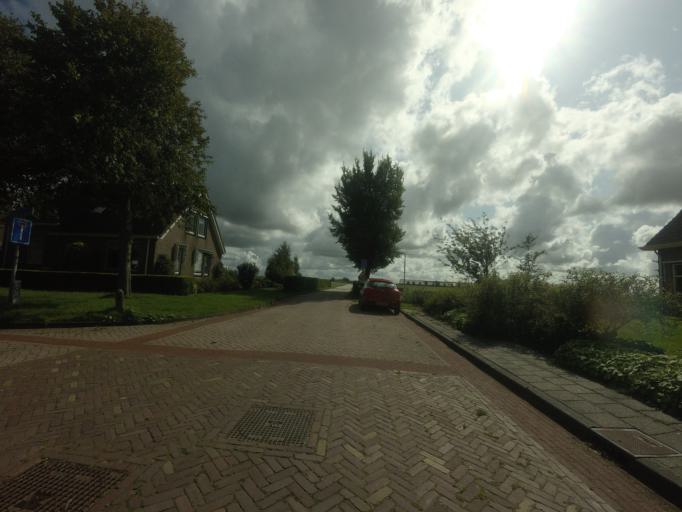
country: NL
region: Friesland
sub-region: Sudwest Fryslan
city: Scharnegoutum
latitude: 53.0754
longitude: 5.6366
